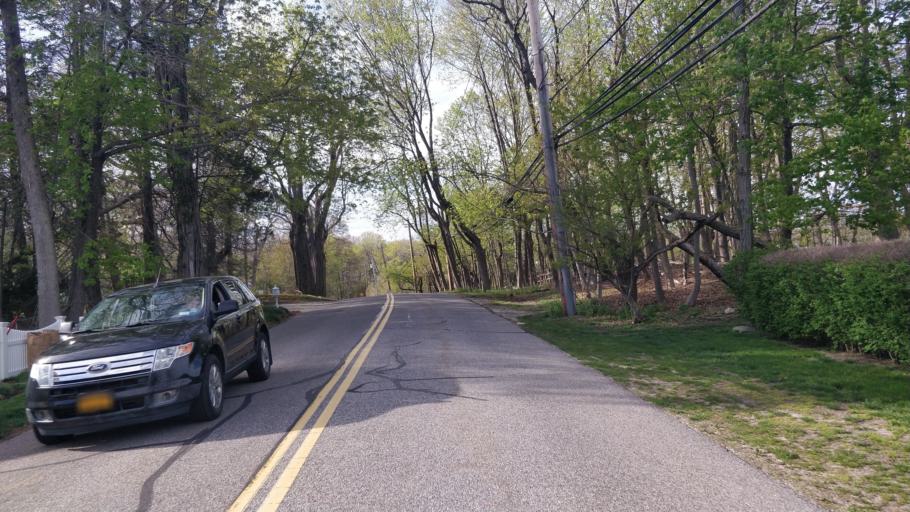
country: US
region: New York
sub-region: Suffolk County
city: East Setauket
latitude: 40.9578
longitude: -73.1281
